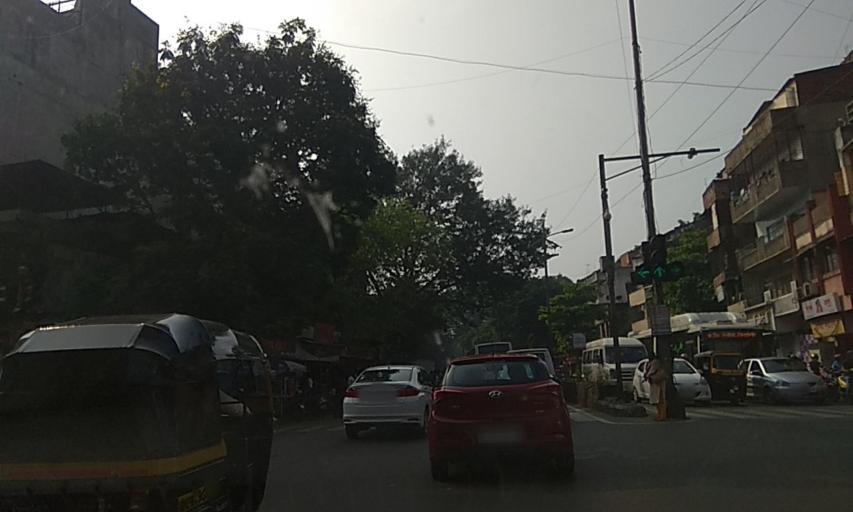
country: IN
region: Maharashtra
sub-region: Pune Division
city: Pune
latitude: 18.5097
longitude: 73.8435
